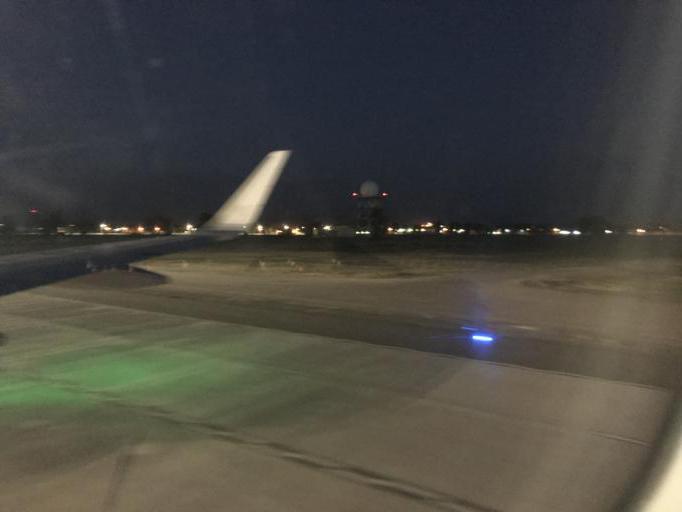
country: AR
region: Mendoza
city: Las Heras
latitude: -32.8268
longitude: -68.7969
